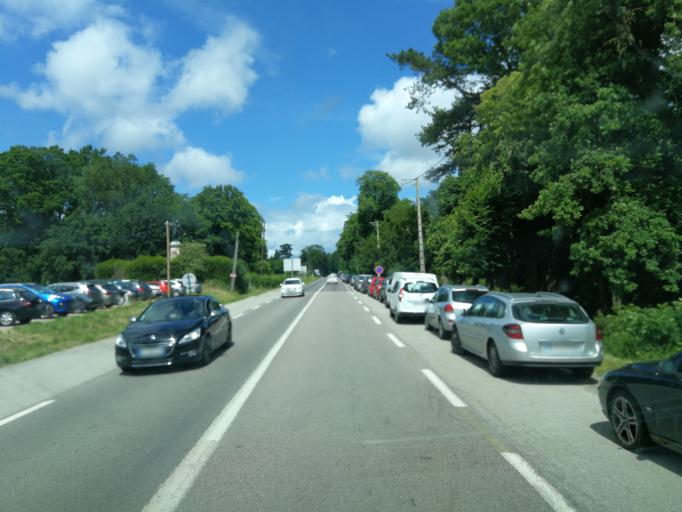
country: FR
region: Haute-Normandie
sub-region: Departement de la Seine-Maritime
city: Sahurs
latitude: 49.3456
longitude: 0.9313
